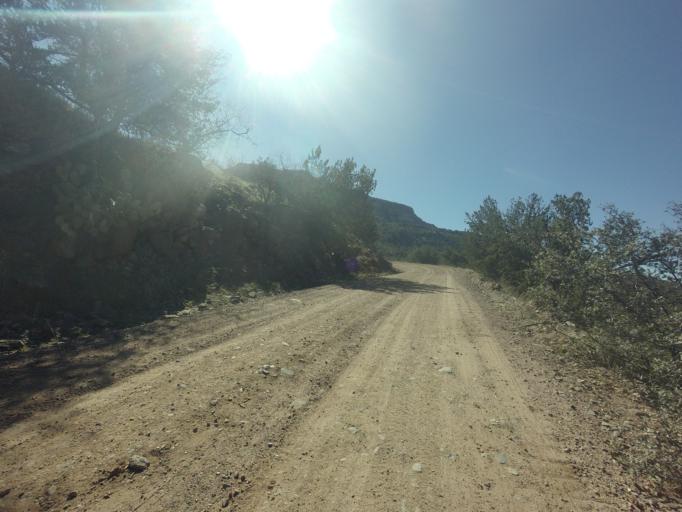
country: US
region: Arizona
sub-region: Gila County
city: Pine
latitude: 34.3940
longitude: -111.6493
